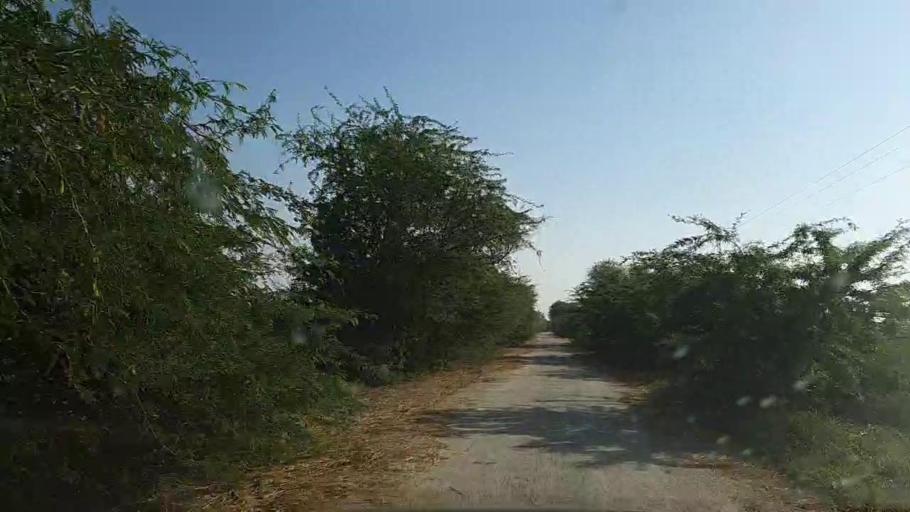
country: PK
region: Sindh
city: Daro Mehar
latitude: 24.6488
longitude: 68.0751
